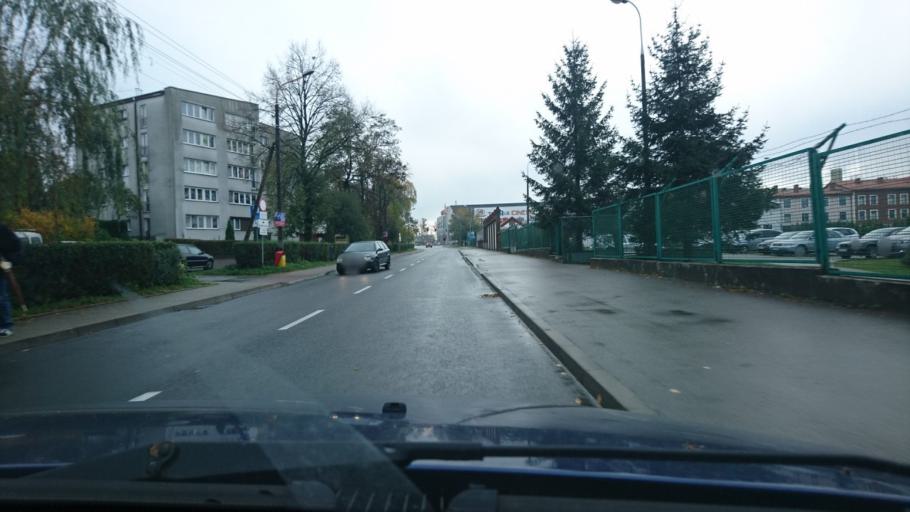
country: PL
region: Silesian Voivodeship
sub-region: Bielsko-Biala
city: Bielsko-Biala
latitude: 49.8058
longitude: 19.0491
